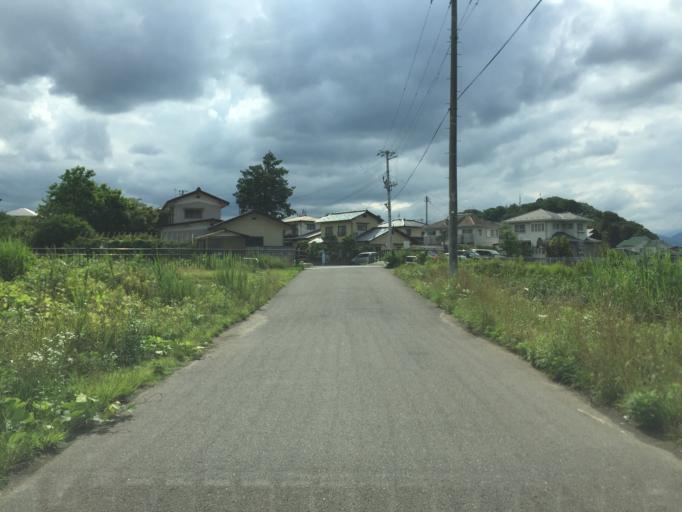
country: JP
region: Fukushima
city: Fukushima-shi
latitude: 37.7439
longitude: 140.4914
